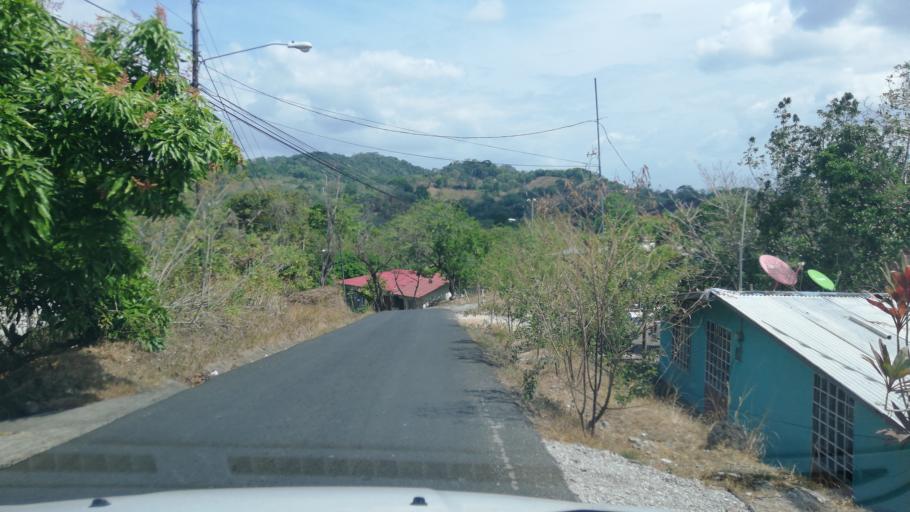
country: PA
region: Panama
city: Alcalde Diaz
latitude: 9.1252
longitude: -79.5641
